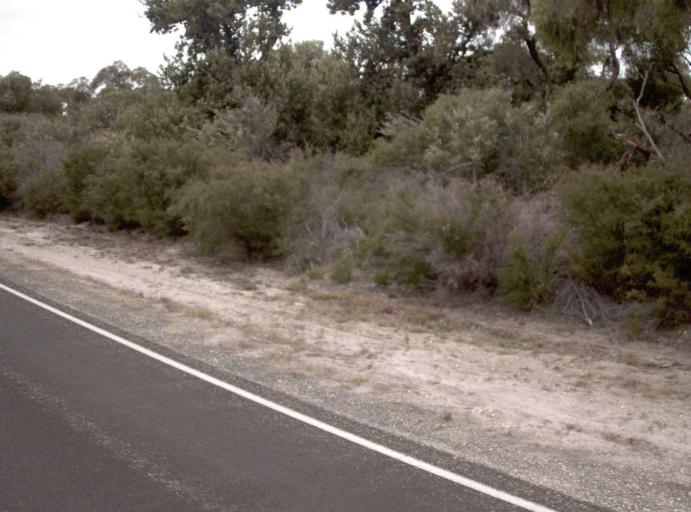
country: AU
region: Victoria
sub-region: Wellington
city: Sale
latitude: -38.1832
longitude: 147.3740
